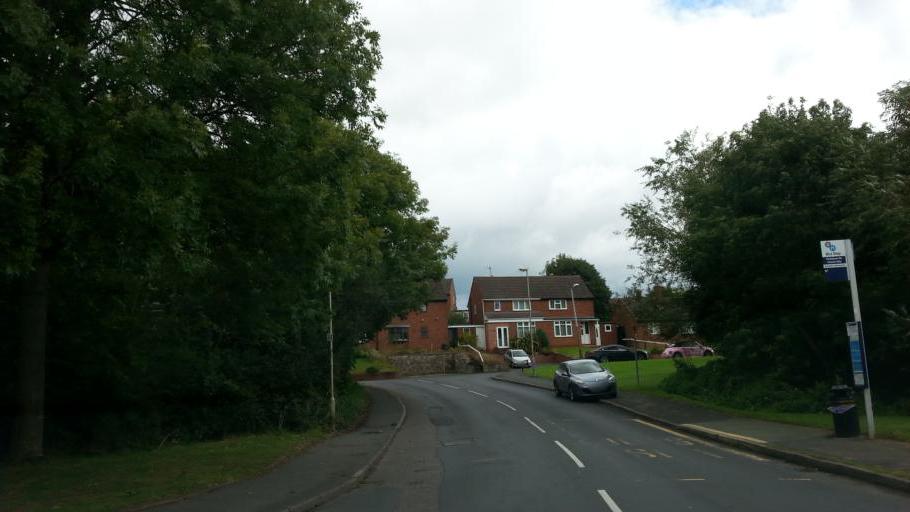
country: GB
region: England
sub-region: Dudley
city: Halesowen
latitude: 52.4423
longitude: -2.0762
